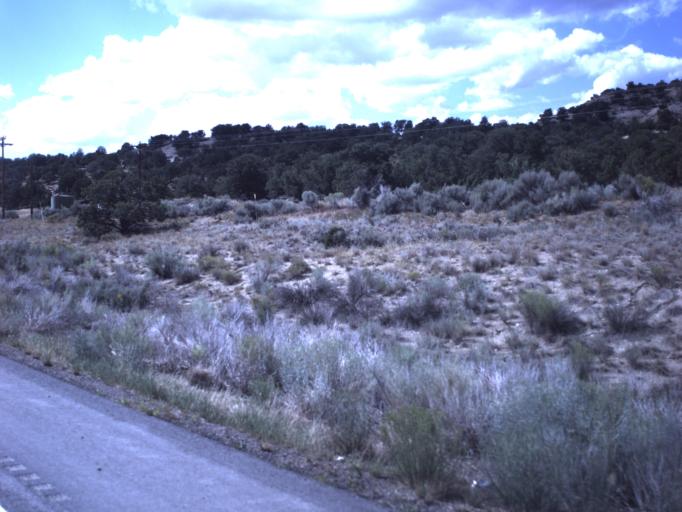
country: US
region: Utah
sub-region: Duchesne County
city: Duchesne
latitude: 40.1724
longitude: -110.5836
